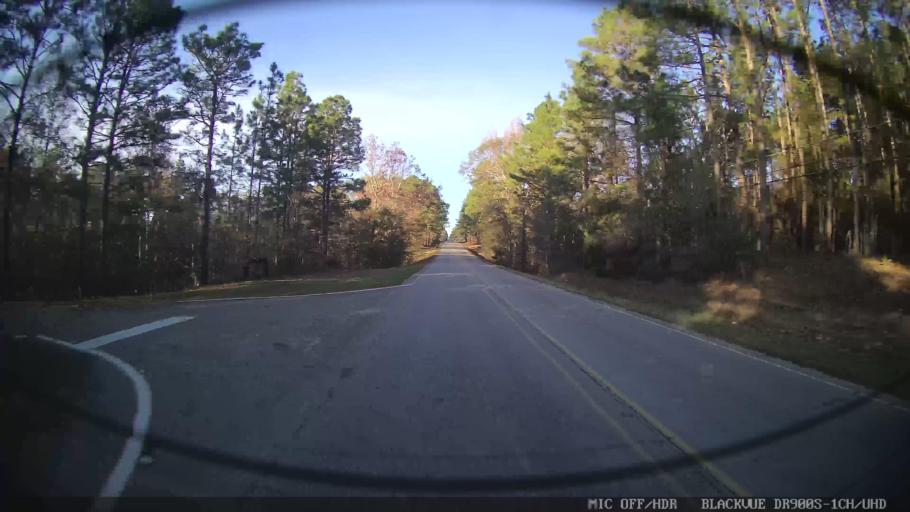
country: US
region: Mississippi
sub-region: Lamar County
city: Purvis
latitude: 31.1216
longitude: -89.4085
